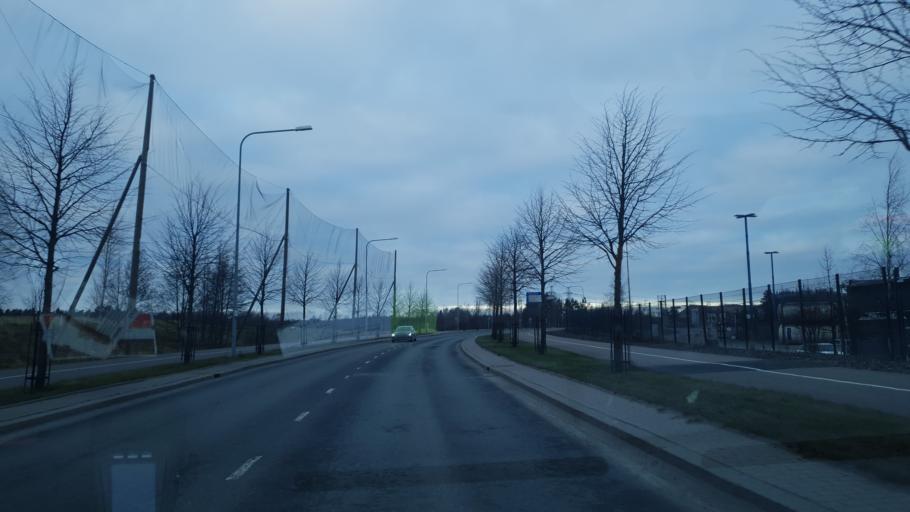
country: FI
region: Uusimaa
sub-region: Helsinki
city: Vantaa
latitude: 60.2147
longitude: 25.1669
